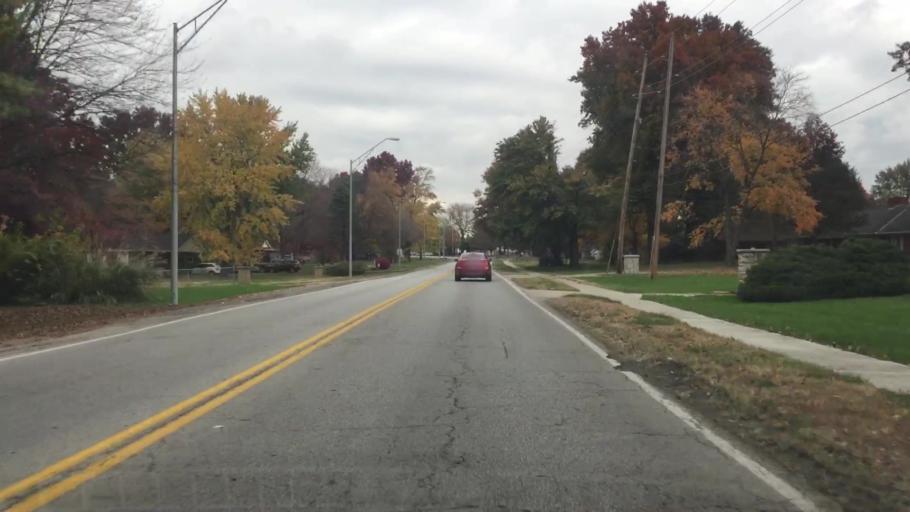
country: US
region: Missouri
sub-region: Jackson County
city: Raytown
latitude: 39.0394
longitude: -94.4371
